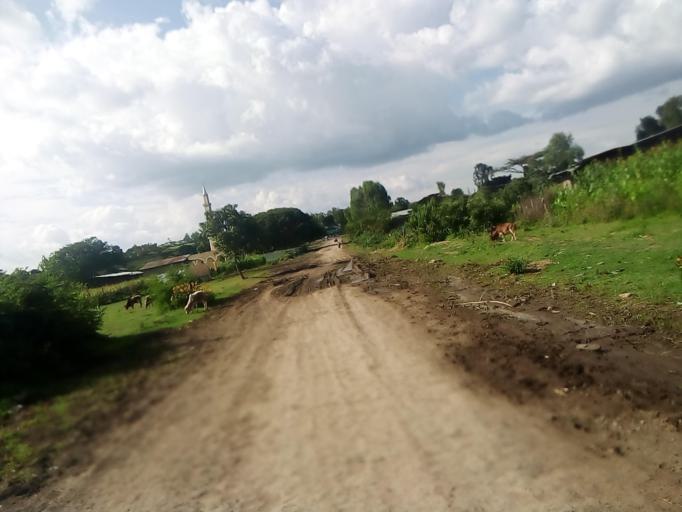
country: ET
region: Southern Nations, Nationalities, and People's Region
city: K'olito
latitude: 7.6636
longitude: 38.0472
